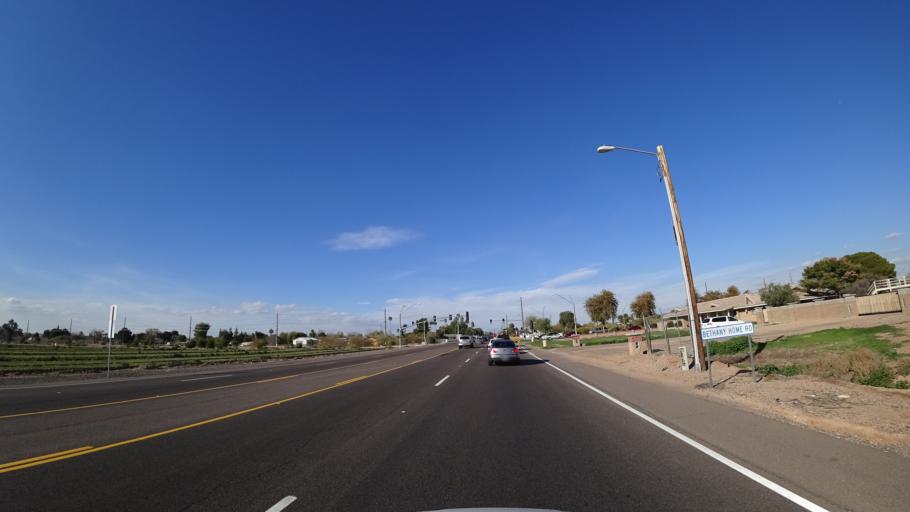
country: US
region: Arizona
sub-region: Maricopa County
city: Glendale
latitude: 33.5214
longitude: -112.2376
